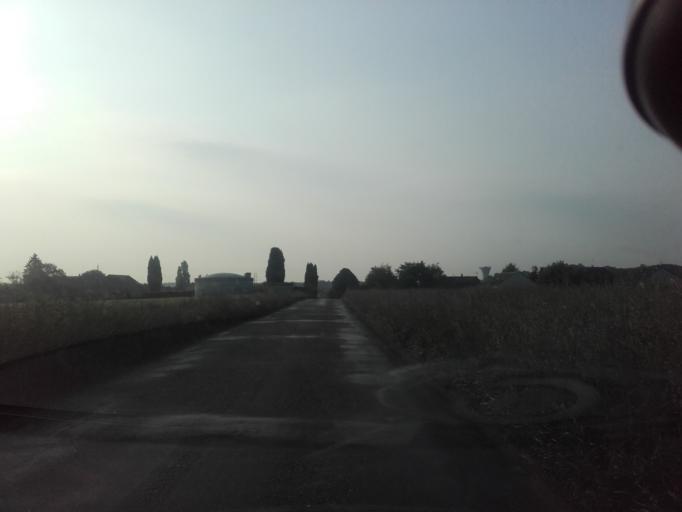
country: FR
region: Centre
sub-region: Departement d'Indre-et-Loire
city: Parcay-Meslay
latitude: 47.4438
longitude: 0.7463
